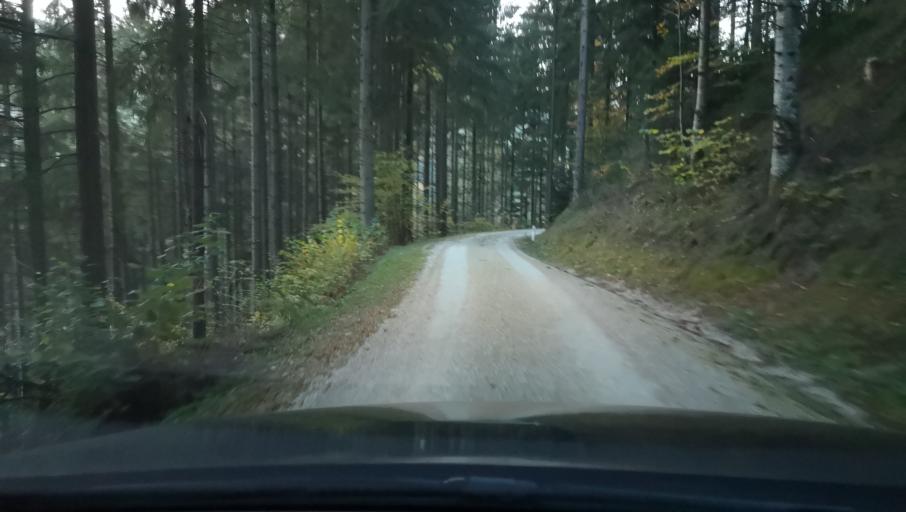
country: AT
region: Styria
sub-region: Politischer Bezirk Weiz
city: Birkfeld
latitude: 47.3651
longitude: 15.6567
